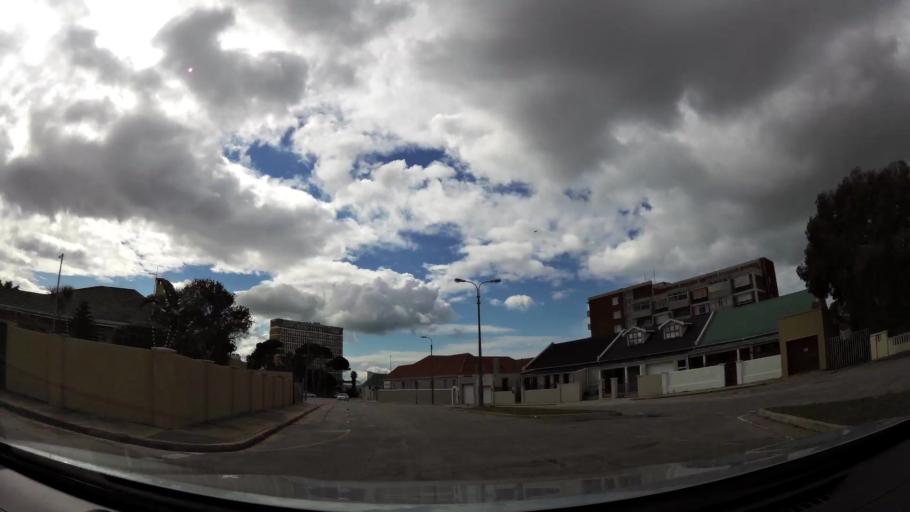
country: ZA
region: Eastern Cape
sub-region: Nelson Mandela Bay Metropolitan Municipality
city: Port Elizabeth
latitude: -33.9610
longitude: 25.5996
